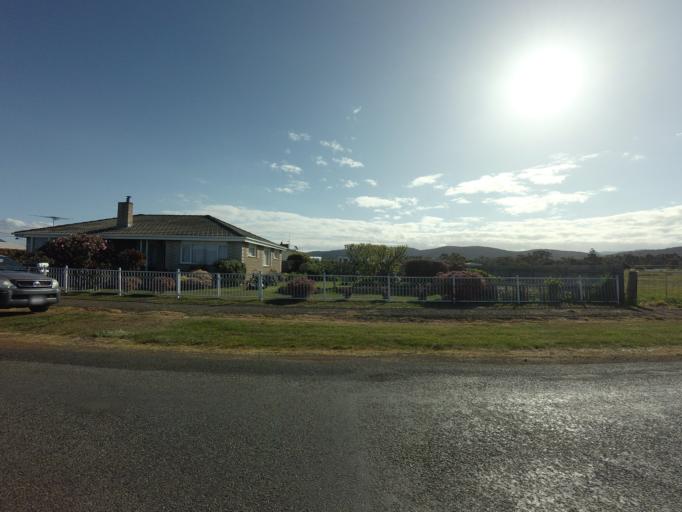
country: AU
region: Tasmania
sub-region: Sorell
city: Sorell
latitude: -42.5053
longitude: 147.9160
